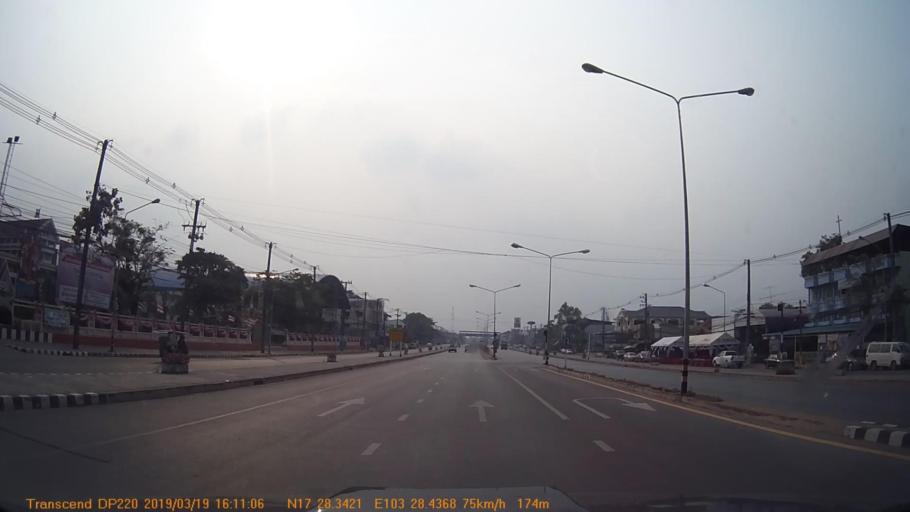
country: TH
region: Sakon Nakhon
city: Sawang Daen Din
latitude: 17.4725
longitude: 103.4733
